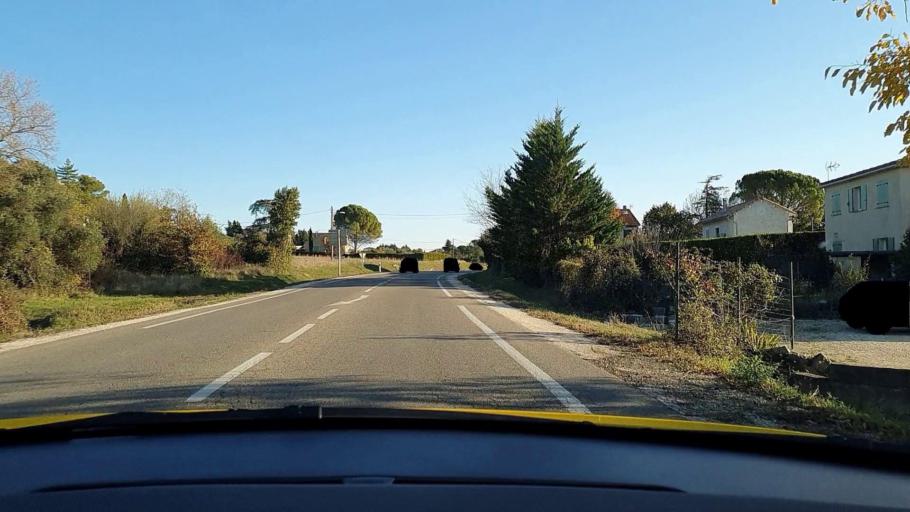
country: FR
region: Languedoc-Roussillon
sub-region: Departement du Gard
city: Saint-Julien-les-Rosiers
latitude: 44.1599
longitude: 4.1178
